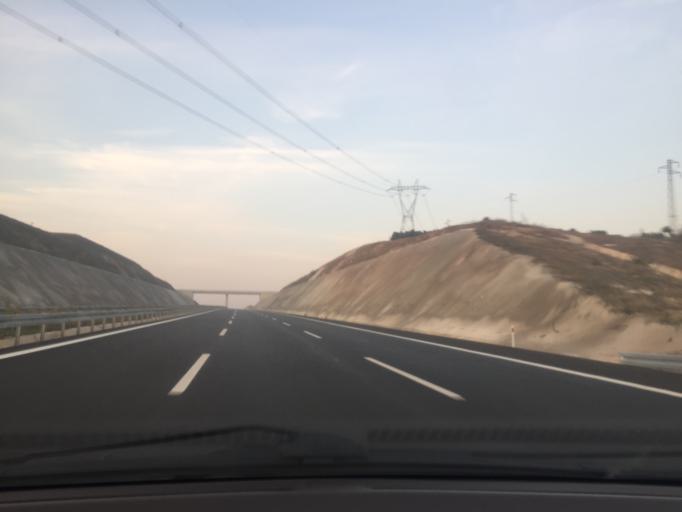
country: TR
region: Bursa
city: Mahmudiye
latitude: 40.2742
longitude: 28.5082
